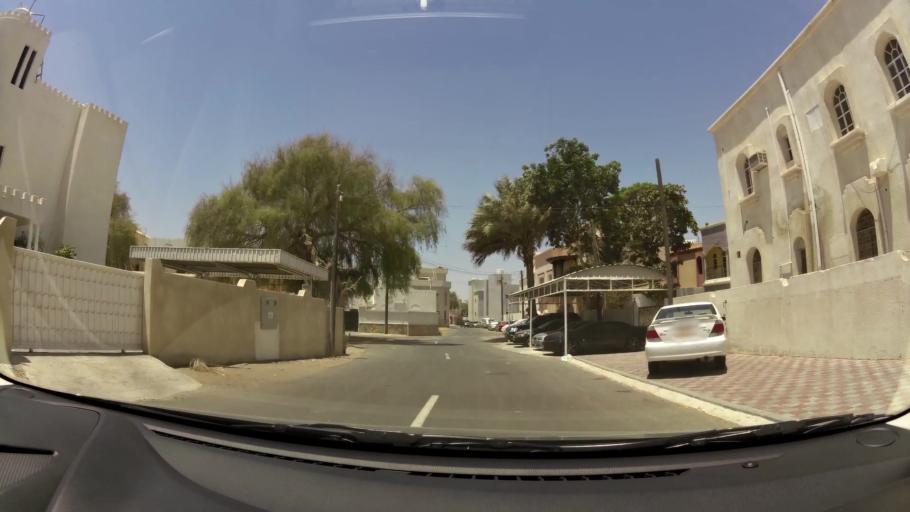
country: OM
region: Muhafazat Masqat
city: As Sib al Jadidah
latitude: 23.6336
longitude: 58.2446
